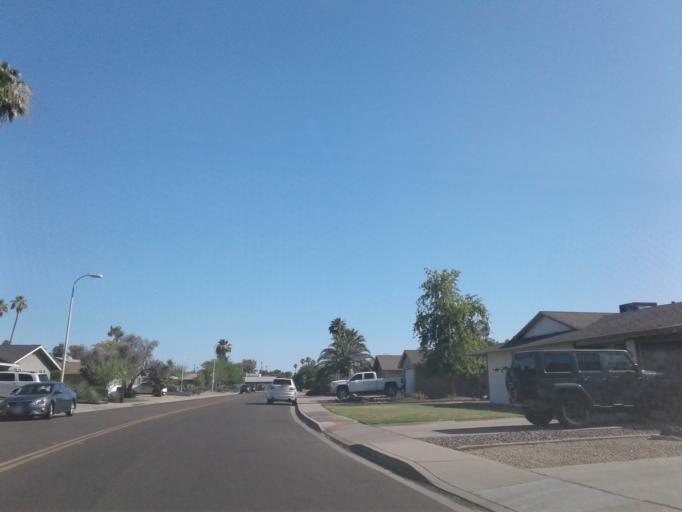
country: US
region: Arizona
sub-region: Maricopa County
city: Scottsdale
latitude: 33.4927
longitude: -111.8951
